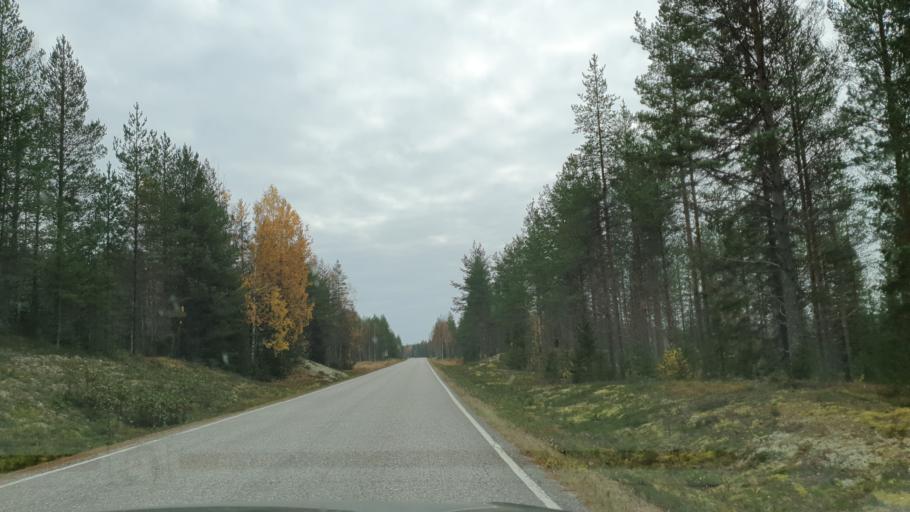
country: FI
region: Kainuu
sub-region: Kajaani
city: Ristijaervi
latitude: 64.6233
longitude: 27.9946
